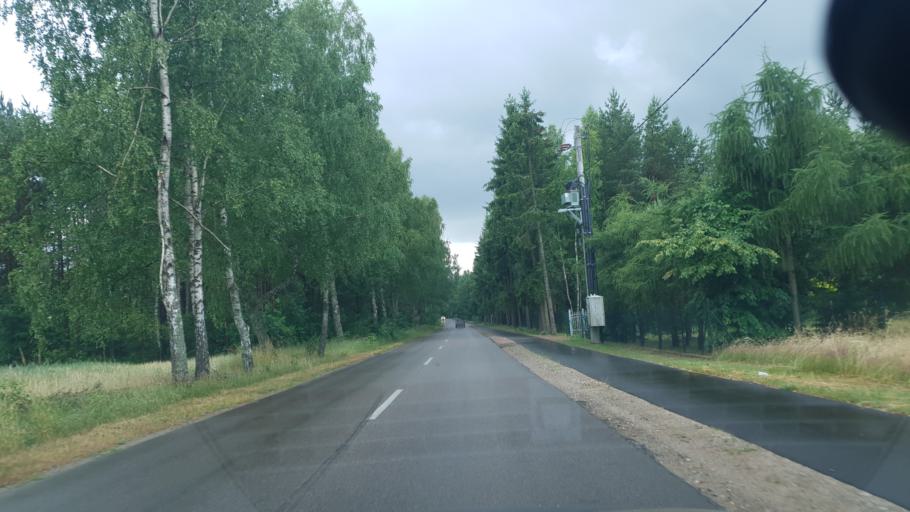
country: PL
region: Pomeranian Voivodeship
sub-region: Powiat kartuski
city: Stezyca
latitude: 54.2319
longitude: 17.9794
